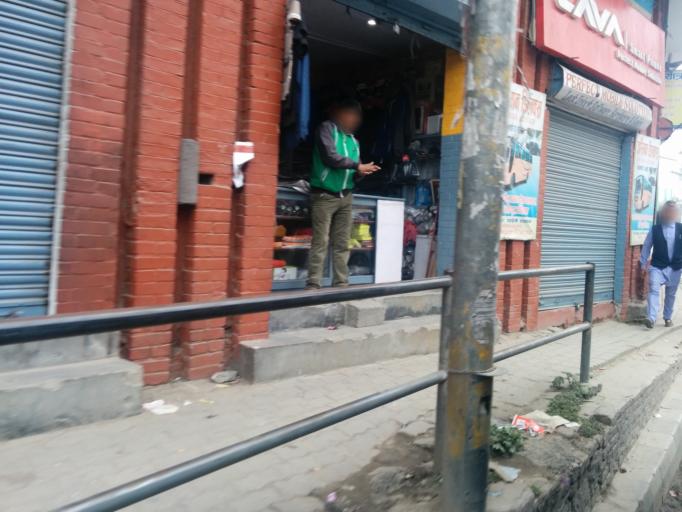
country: NP
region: Central Region
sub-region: Bagmati Zone
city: Kathmandu
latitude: 27.7079
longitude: 85.3430
